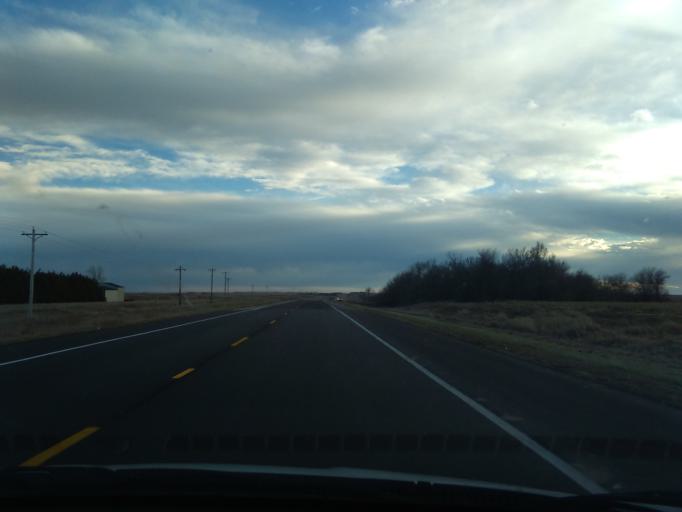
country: US
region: Nebraska
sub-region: Phelps County
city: Holdrege
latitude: 40.3678
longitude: -99.3693
